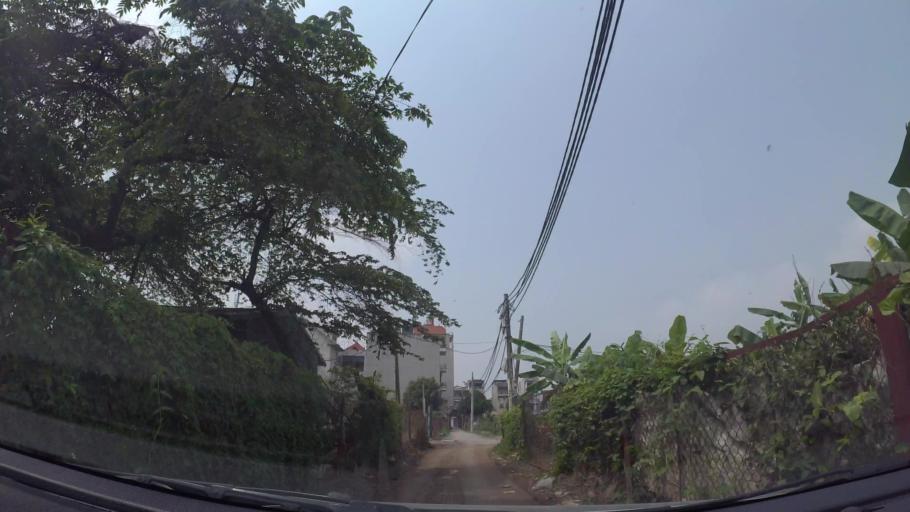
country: VN
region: Ha Noi
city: Tay Ho
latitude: 21.0862
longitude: 105.8002
